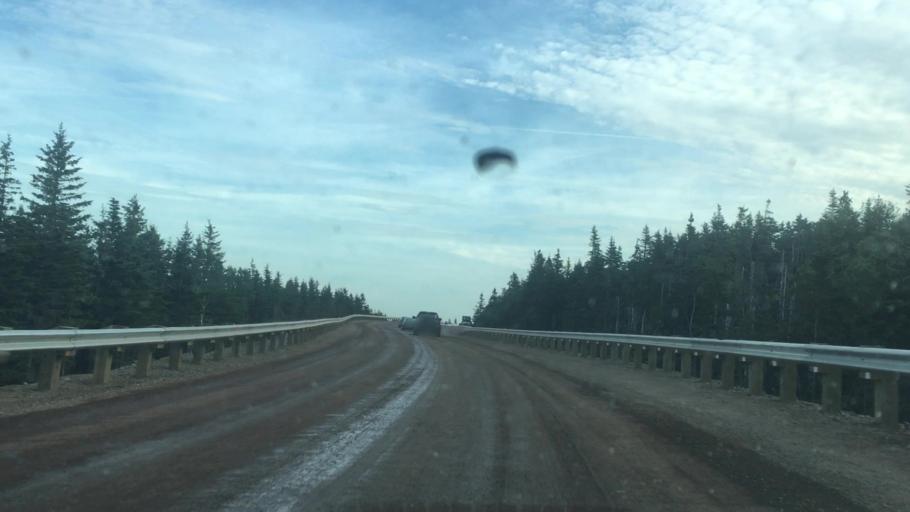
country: CA
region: Nova Scotia
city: Sydney Mines
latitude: 46.8056
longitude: -60.8443
